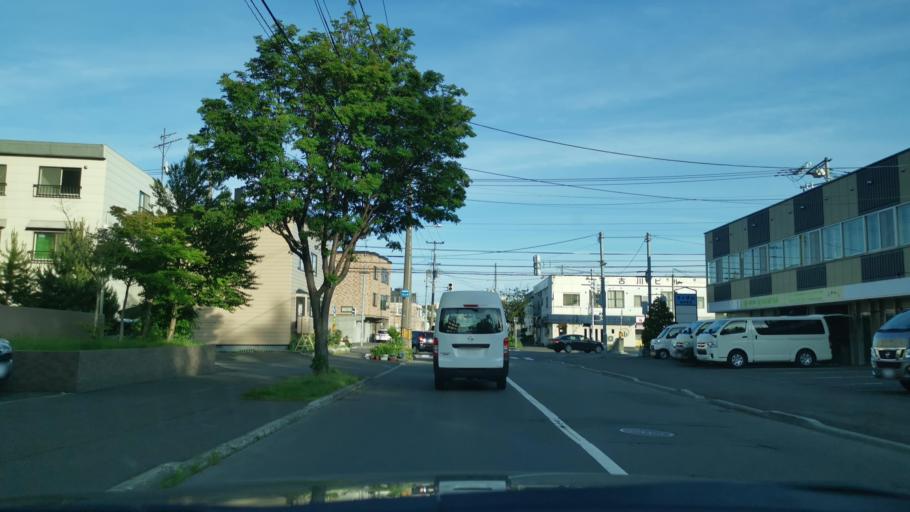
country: JP
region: Hokkaido
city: Sapporo
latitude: 43.0700
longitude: 141.4032
